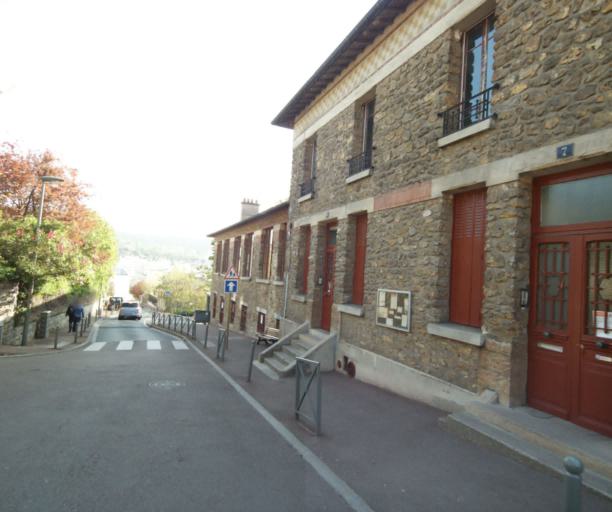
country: FR
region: Ile-de-France
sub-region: Departement des Hauts-de-Seine
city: Sevres
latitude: 48.8261
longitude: 2.2084
